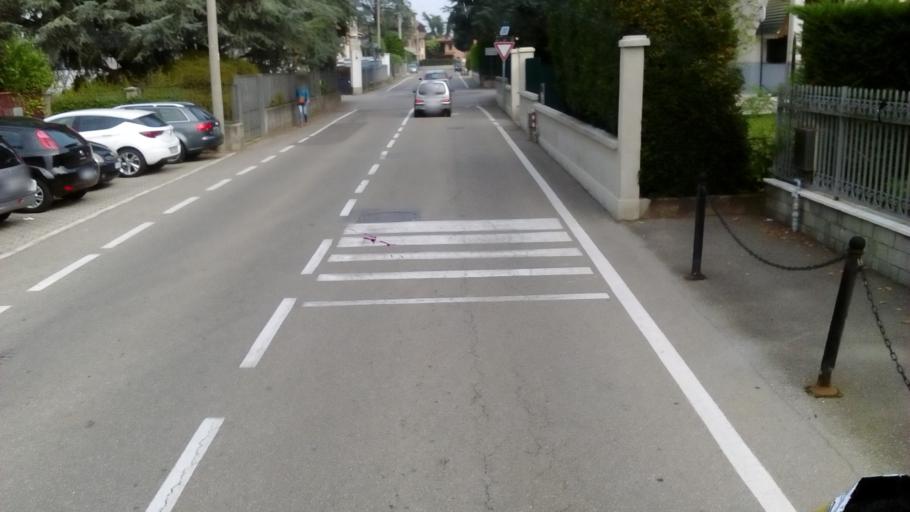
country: IT
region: Lombardy
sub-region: Provincia di Como
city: Rovellasca
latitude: 45.6692
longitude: 9.0456
